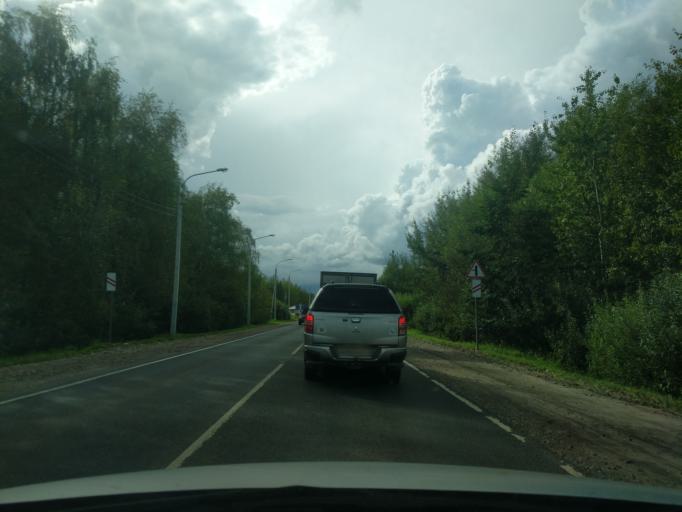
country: RU
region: Jaroslavl
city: Yaroslavl
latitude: 57.5433
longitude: 39.9396
